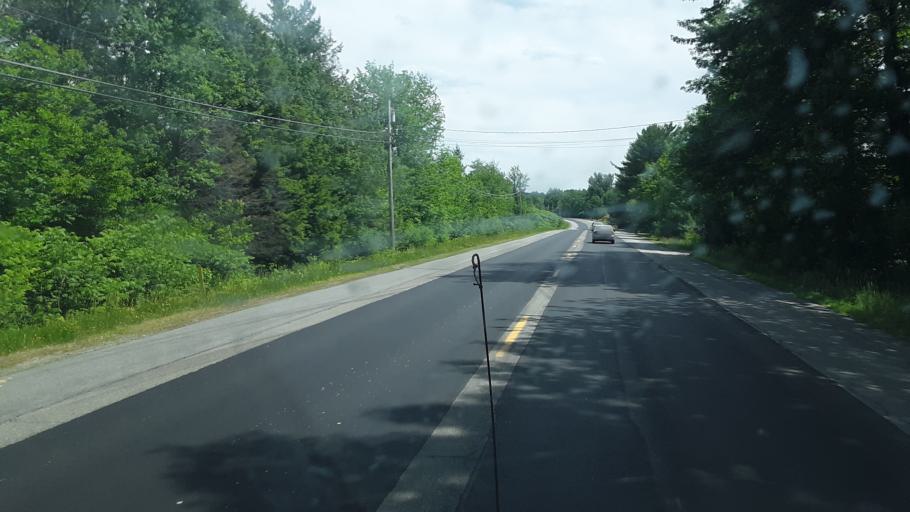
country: US
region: Maine
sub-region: Kennebec County
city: Oakland
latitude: 44.6434
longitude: -69.6919
